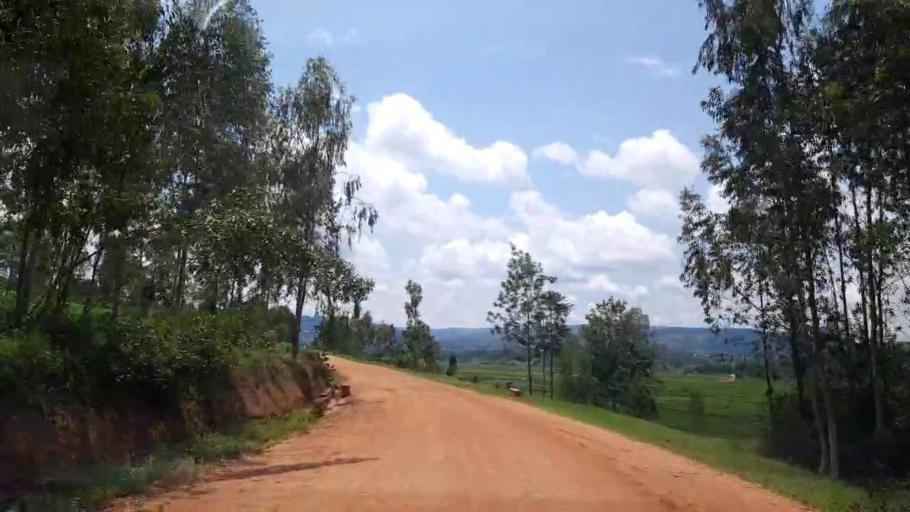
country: RW
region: Northern Province
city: Byumba
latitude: -1.5679
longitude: 30.2972
